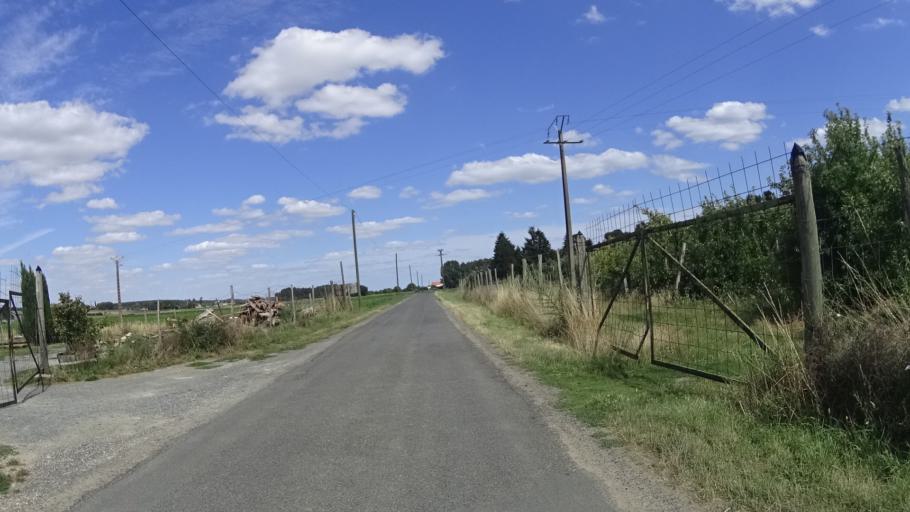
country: FR
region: Centre
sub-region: Departement d'Indre-et-Loire
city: Vernou-sur-Brenne
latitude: 47.3995
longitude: 0.8487
